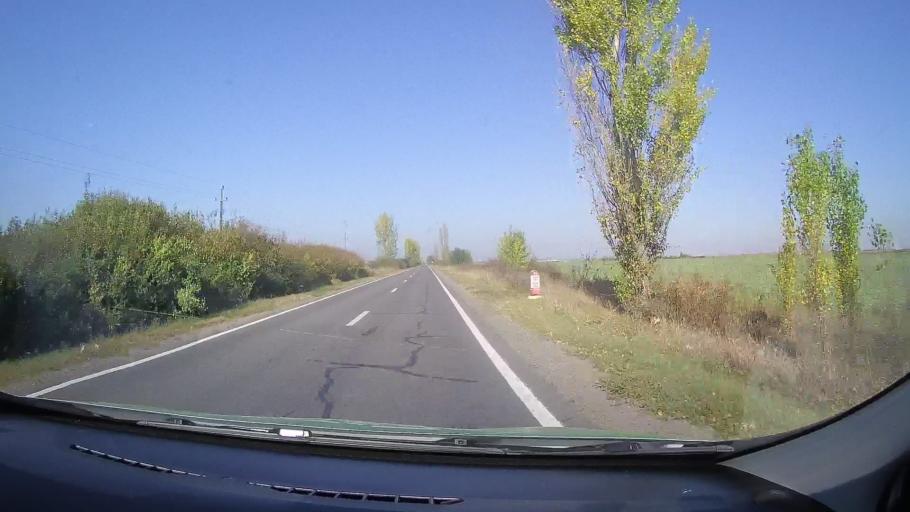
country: RO
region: Satu Mare
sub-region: Comuna Urziceni
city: Urziceni
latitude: 47.7093
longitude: 22.4288
